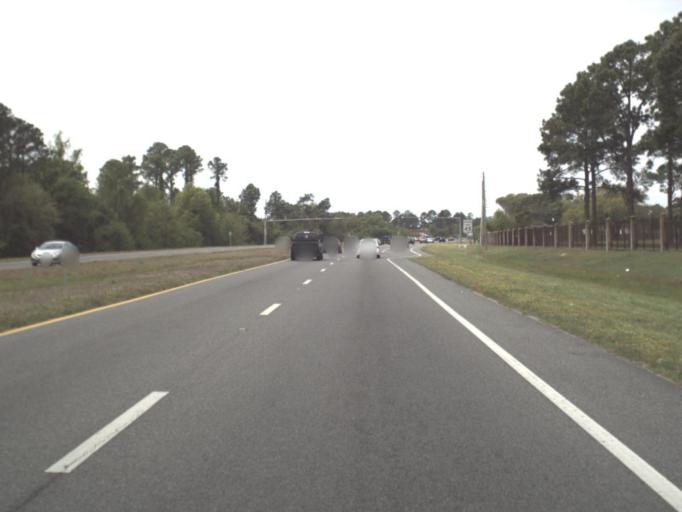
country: US
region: Florida
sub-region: Escambia County
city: Myrtle Grove
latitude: 30.3969
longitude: -87.2987
